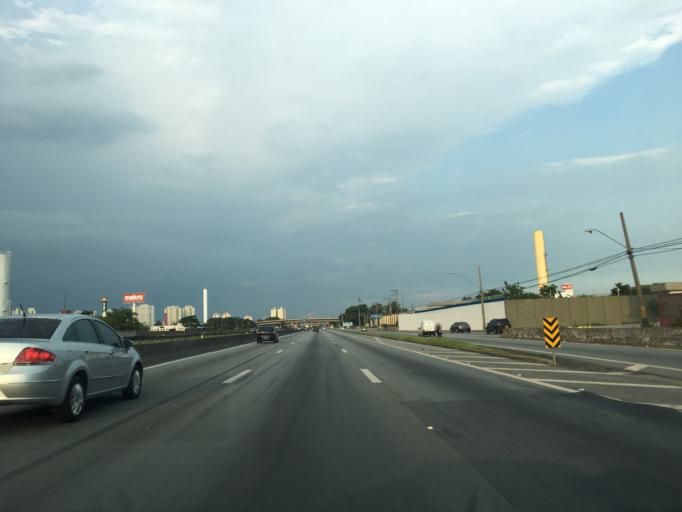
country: BR
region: Sao Paulo
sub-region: Guarulhos
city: Guarulhos
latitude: -23.4811
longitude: -46.5333
